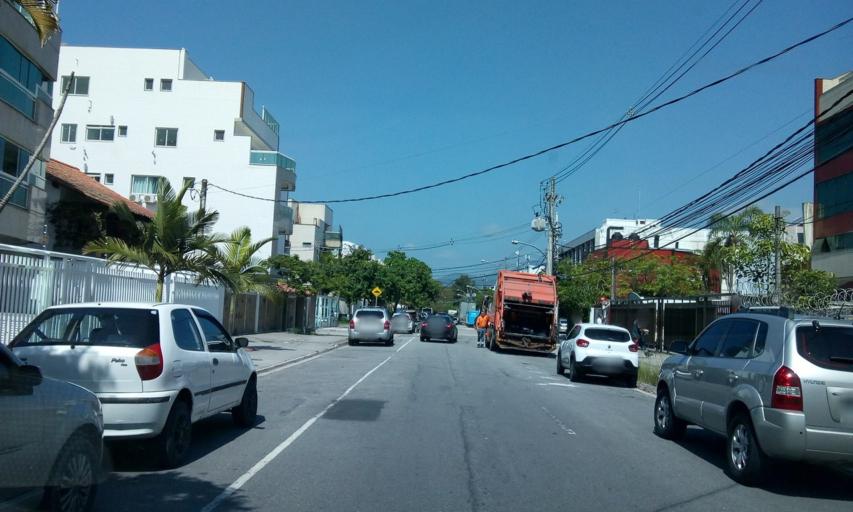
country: BR
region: Rio de Janeiro
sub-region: Nilopolis
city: Nilopolis
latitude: -23.0159
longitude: -43.4693
